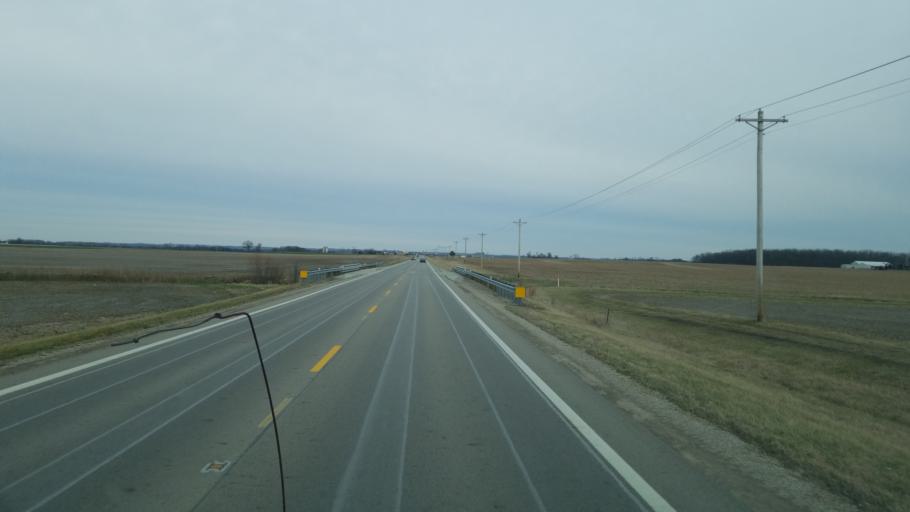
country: US
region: Ohio
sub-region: Pickaway County
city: Logan Elm Village
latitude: 39.5889
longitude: -83.0178
